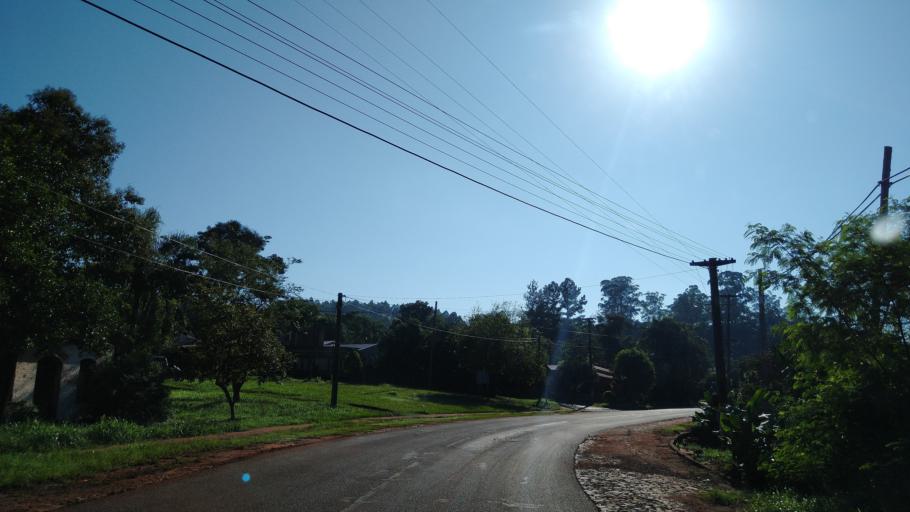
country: AR
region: Misiones
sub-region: Departamento de Montecarlo
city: Montecarlo
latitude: -26.5611
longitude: -54.7809
